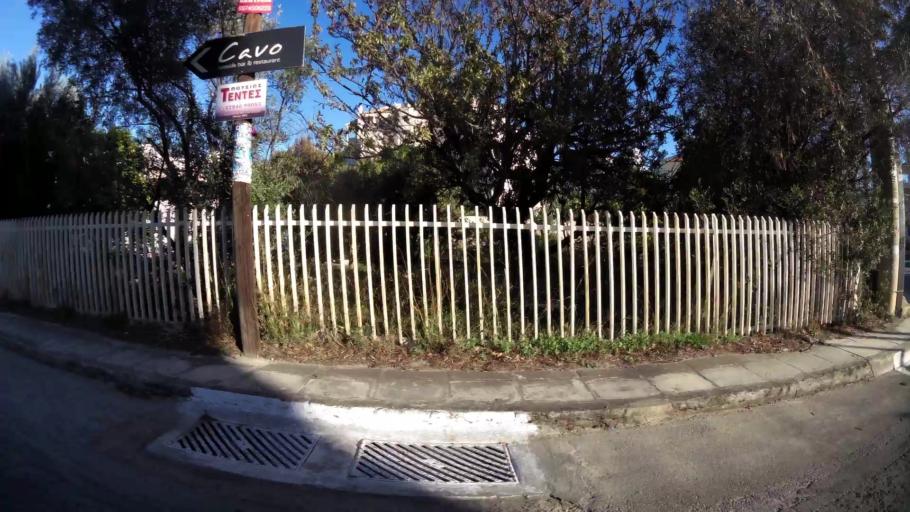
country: GR
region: Attica
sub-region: Nomarchia Anatolikis Attikis
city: Rafina
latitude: 38.0279
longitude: 23.9987
